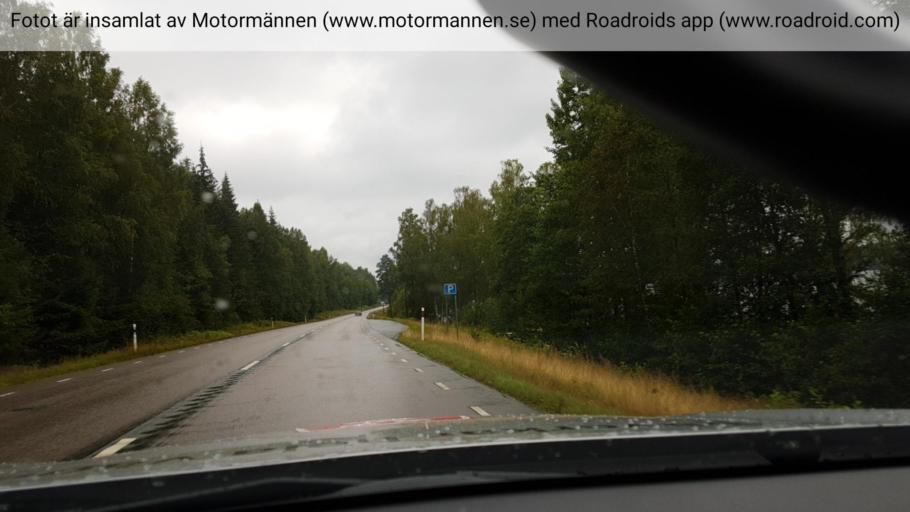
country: SE
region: Vaestra Goetaland
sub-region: Bengtsfors Kommun
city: Billingsfors
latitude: 58.9344
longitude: 12.1278
